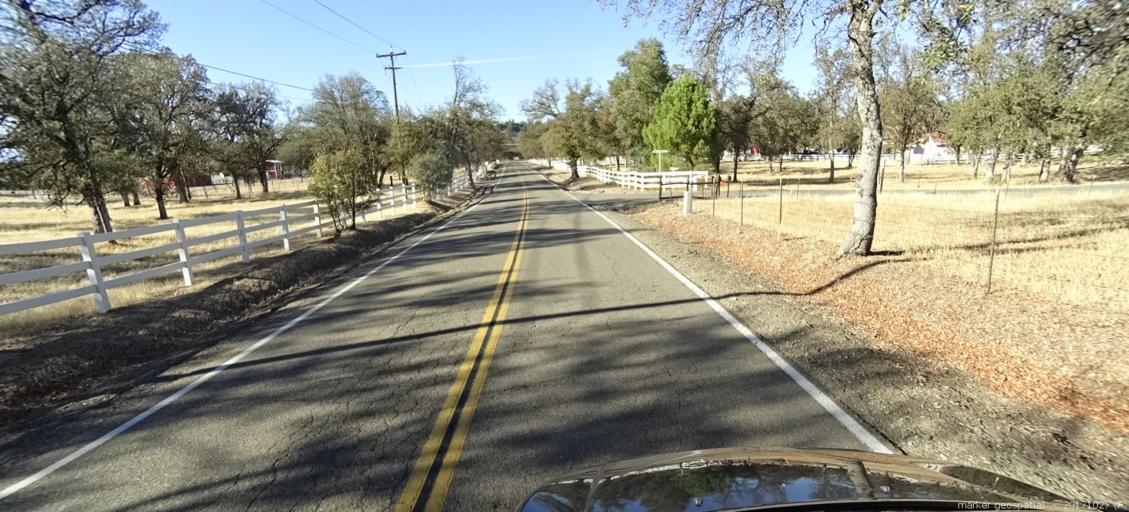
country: US
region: California
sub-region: Shasta County
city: Palo Cedro
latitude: 40.5612
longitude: -122.1891
